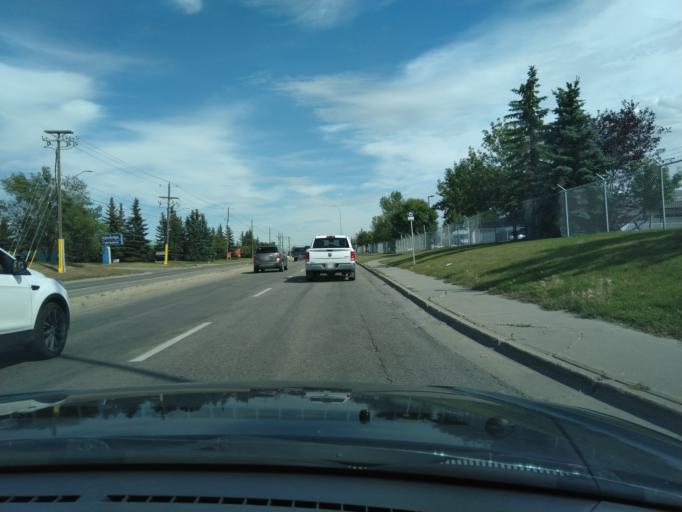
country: CA
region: Alberta
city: Calgary
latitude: 51.0768
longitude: -113.9980
